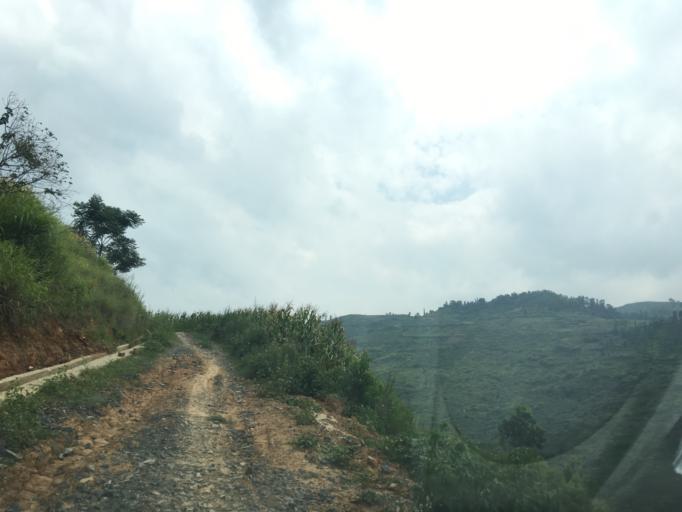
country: CN
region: Guangxi Zhuangzu Zizhiqu
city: Xinzhou
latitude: 25.1978
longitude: 105.7332
